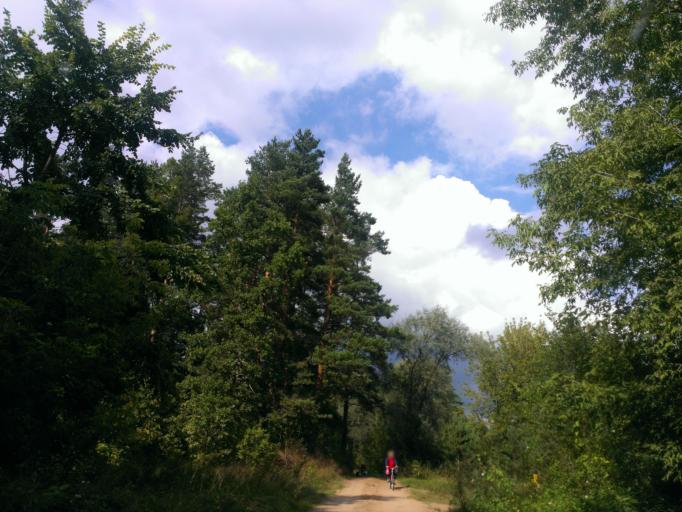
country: LV
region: Garkalne
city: Garkalne
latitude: 56.9714
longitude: 24.4850
